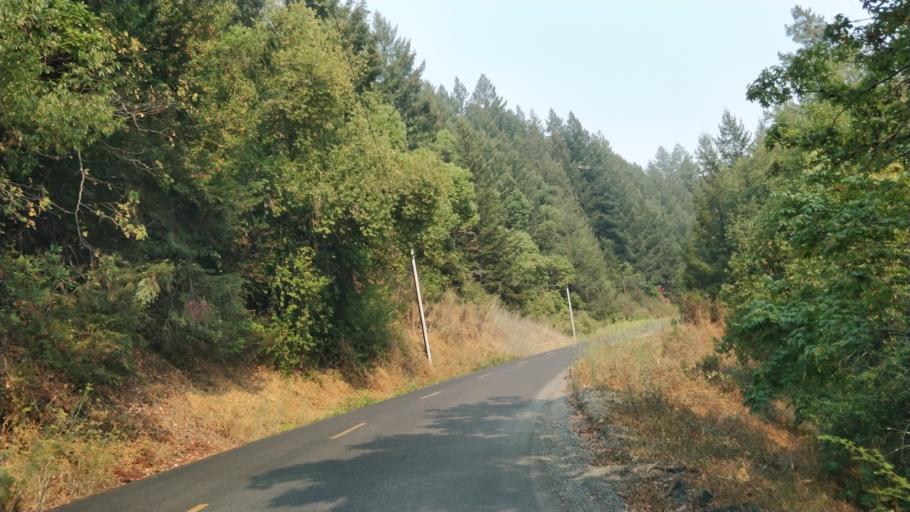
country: US
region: California
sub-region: Humboldt County
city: Rio Dell
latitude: 40.2697
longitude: -124.2220
